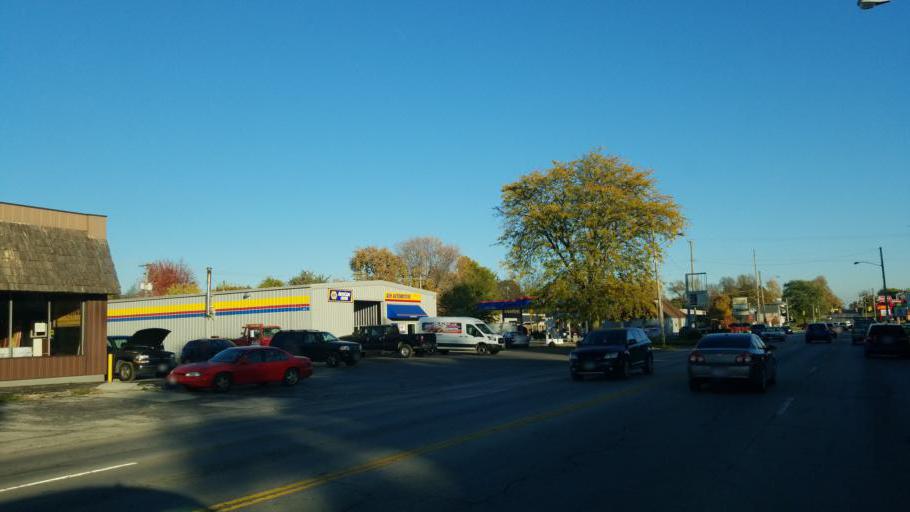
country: US
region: Ohio
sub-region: Sandusky County
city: Fremont
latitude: 41.3457
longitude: -83.1069
